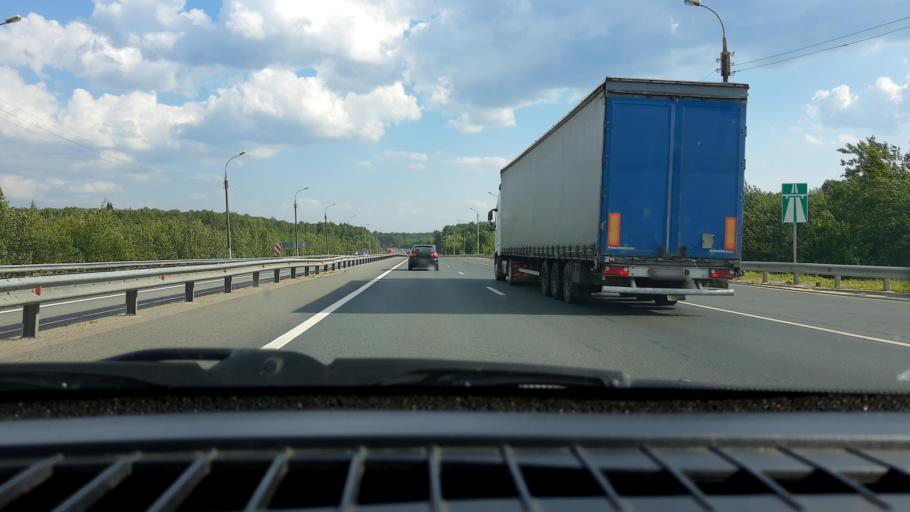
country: RU
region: Nizjnij Novgorod
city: Gorbatovka
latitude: 56.2590
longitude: 43.7082
